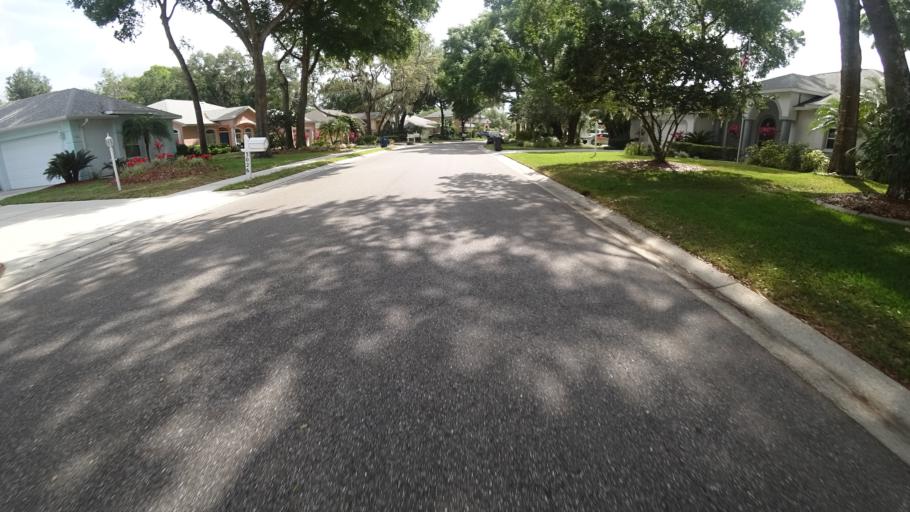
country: US
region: Florida
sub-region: Manatee County
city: Ellenton
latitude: 27.5404
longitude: -82.4498
